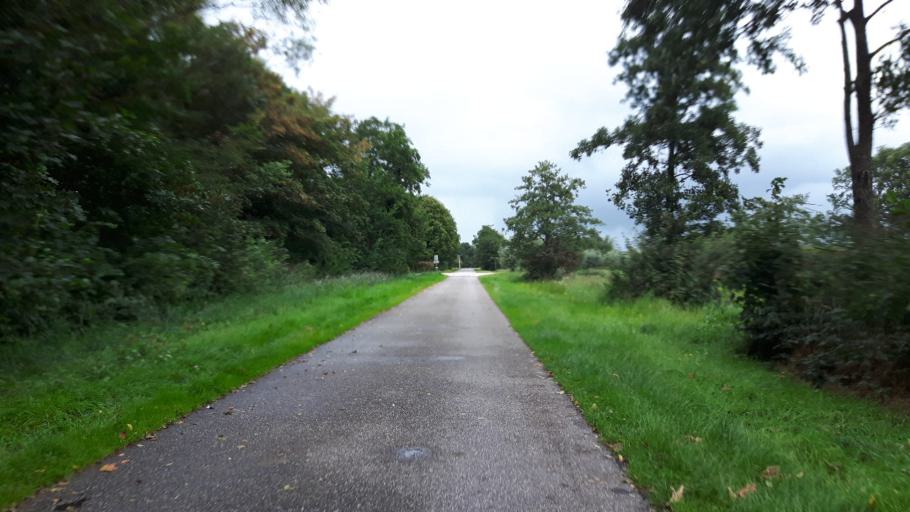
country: NL
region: Friesland
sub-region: Gemeente Dantumadiel
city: Broeksterwald
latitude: 53.2695
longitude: 5.9826
